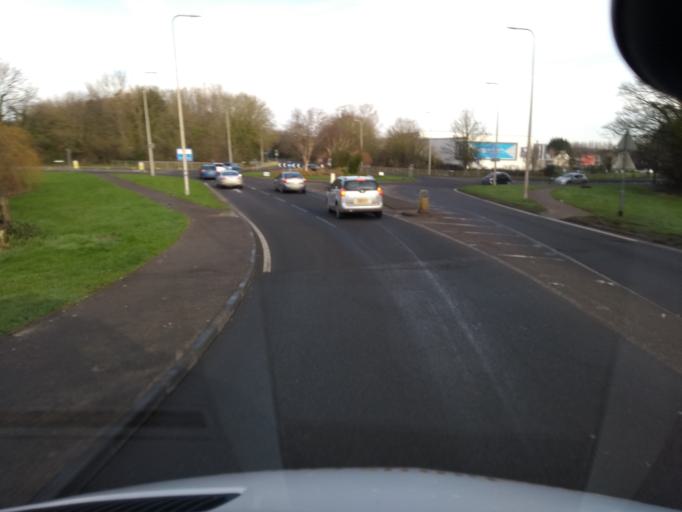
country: GB
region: England
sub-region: North Somerset
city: Bleadon
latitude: 51.3207
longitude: -2.9688
